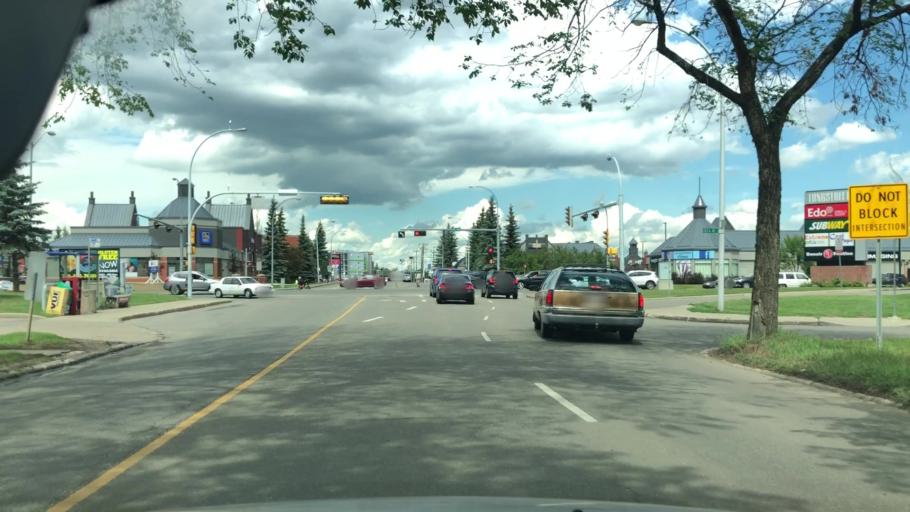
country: CA
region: Alberta
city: Edmonton
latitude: 53.5455
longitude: -113.5213
